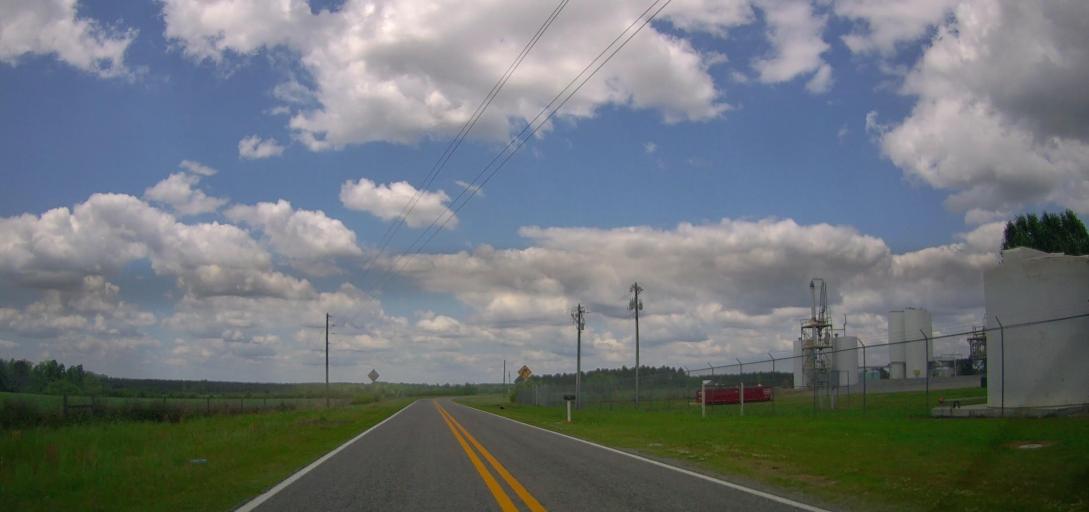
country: US
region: Georgia
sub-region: Laurens County
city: East Dublin
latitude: 32.5430
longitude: -82.8167
